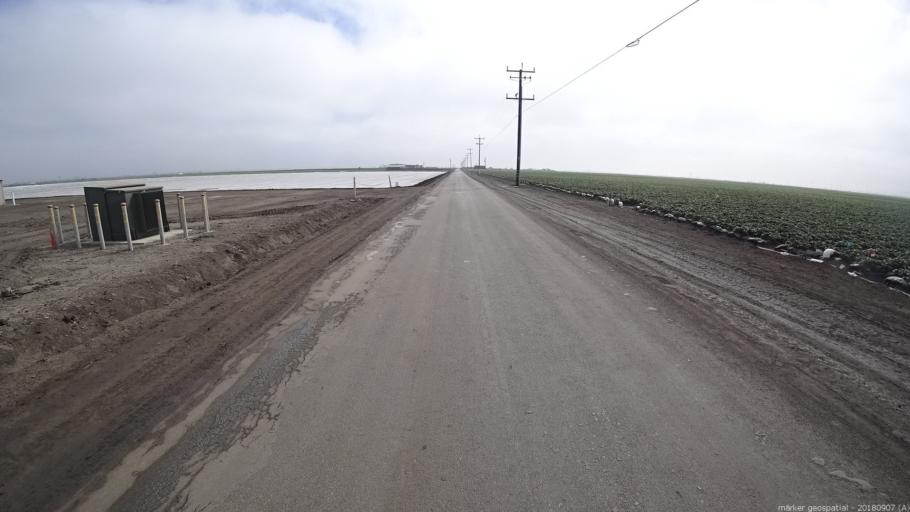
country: US
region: California
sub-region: Monterey County
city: Boronda
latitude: 36.6932
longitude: -121.7239
